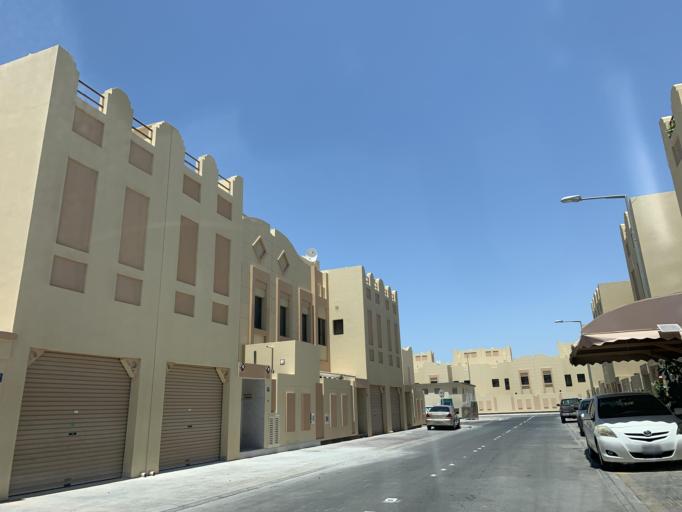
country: BH
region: Manama
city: Jidd Hafs
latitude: 26.2320
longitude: 50.4915
